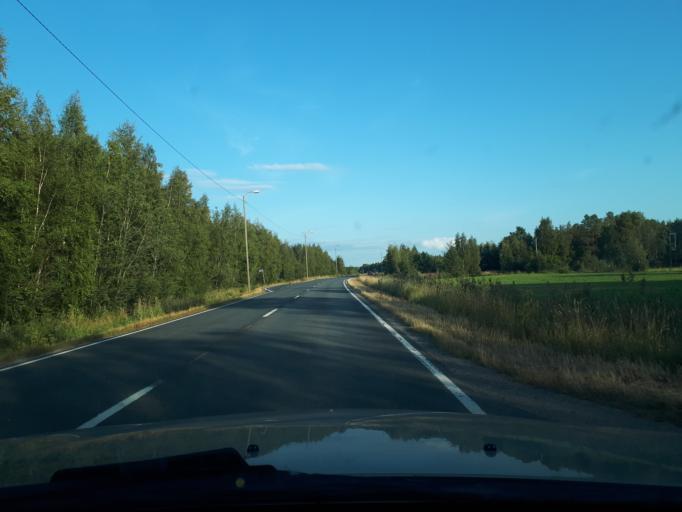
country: FI
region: Northern Ostrobothnia
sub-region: Oulu
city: Oulunsalo
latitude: 64.9836
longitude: 25.2680
